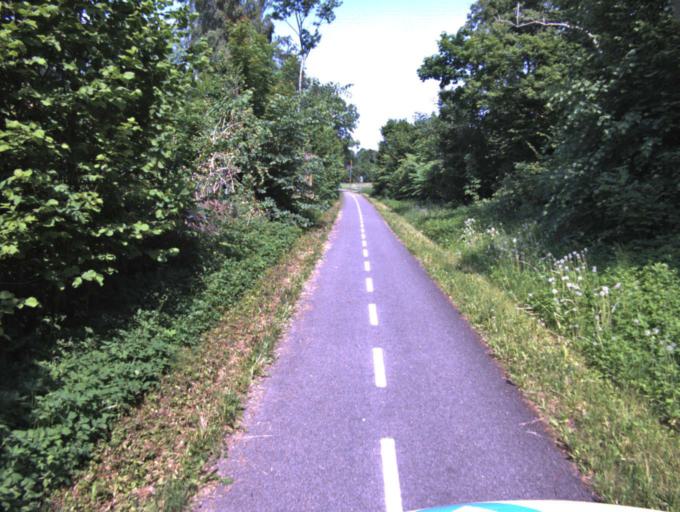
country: SE
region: Skane
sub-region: Kristianstads Kommun
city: Fjalkinge
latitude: 56.0861
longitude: 14.2314
